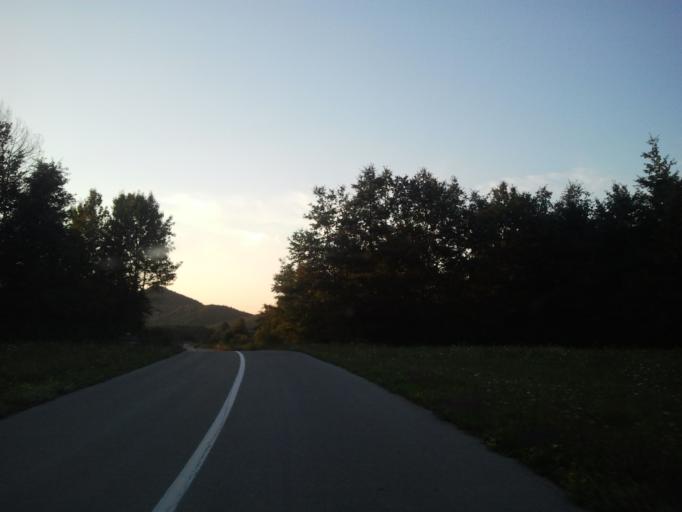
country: HR
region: Zadarska
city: Obrovac
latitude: 44.4153
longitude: 15.6648
